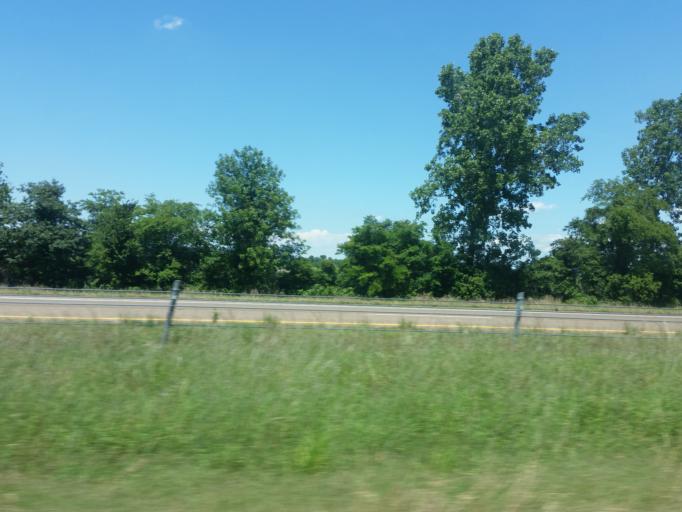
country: US
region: Missouri
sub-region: Pemiscot County
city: Caruthersville
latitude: 36.0908
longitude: -89.5756
